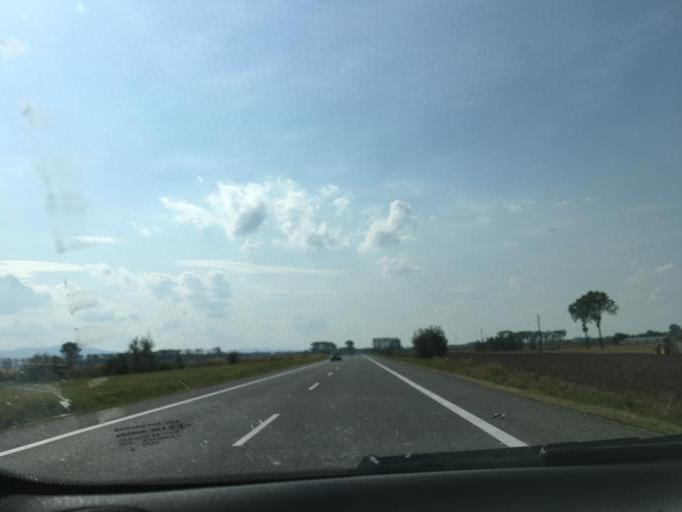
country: PL
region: Opole Voivodeship
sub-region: Powiat prudnicki
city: Lubrza
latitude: 50.3293
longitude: 17.6370
